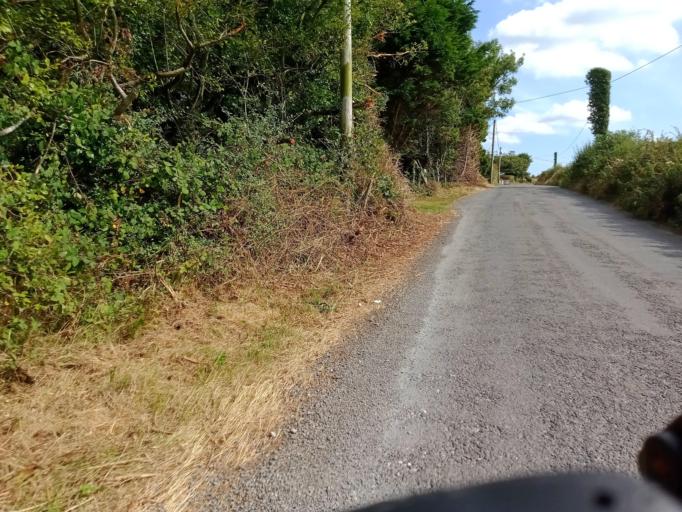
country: IE
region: Munster
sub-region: Waterford
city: Dungarvan
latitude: 52.1176
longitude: -7.4979
